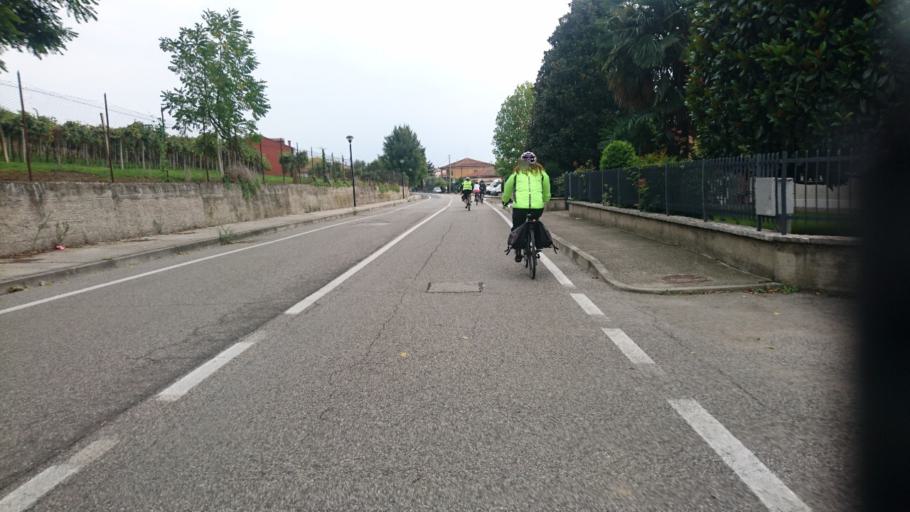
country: IT
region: Veneto
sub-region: Provincia di Verona
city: Caldiero
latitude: 45.4091
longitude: 11.1780
